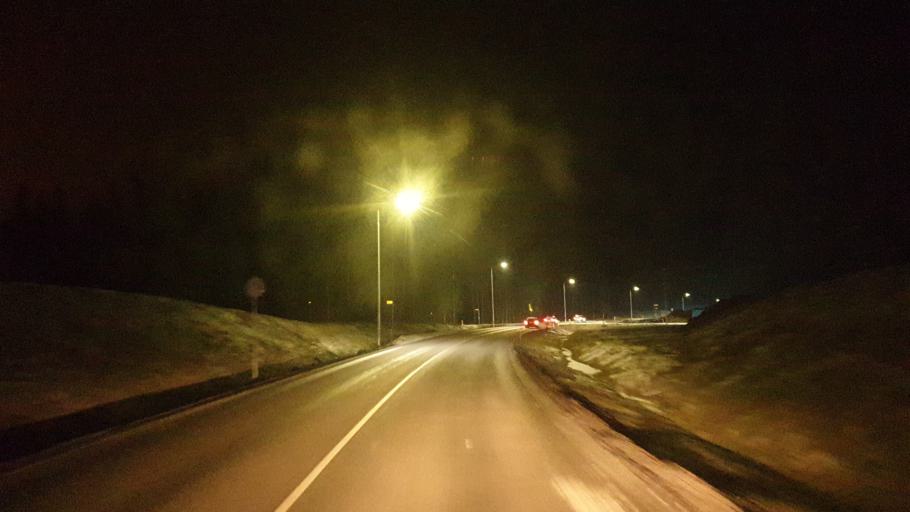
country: FI
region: Southern Savonia
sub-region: Pieksaemaeki
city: Juva
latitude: 61.8588
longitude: 27.7186
